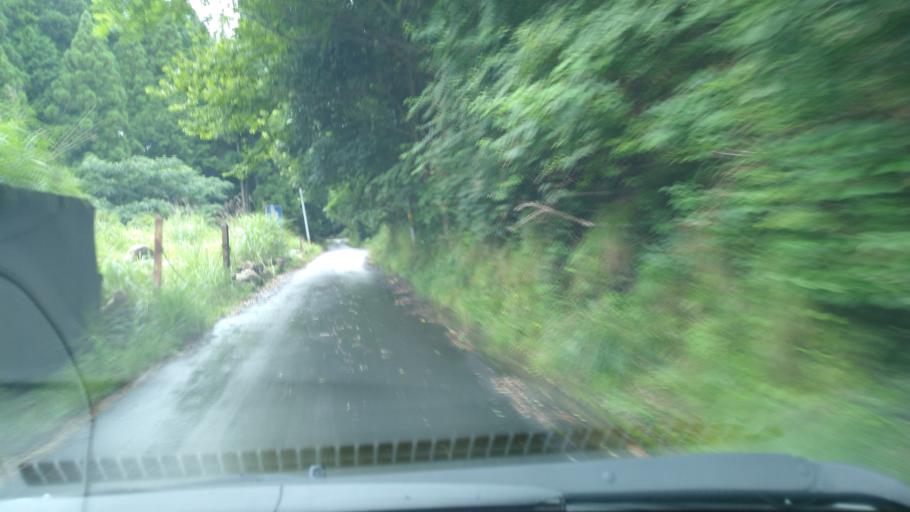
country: JP
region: Kyoto
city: Ayabe
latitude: 35.2262
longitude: 135.2817
